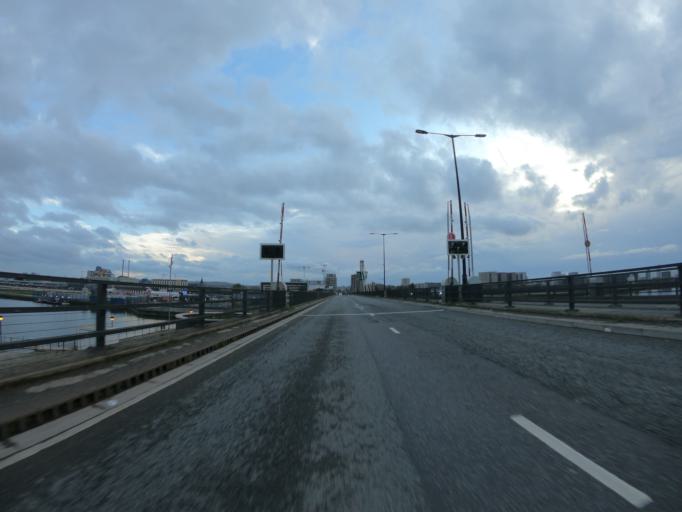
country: GB
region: England
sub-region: Greater London
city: East Ham
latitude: 51.5074
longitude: 0.0401
